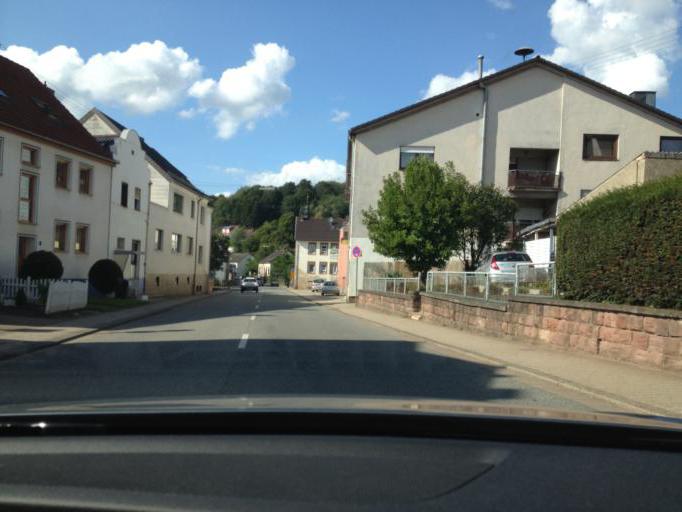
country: DE
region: Saarland
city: Eppelborn
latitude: 49.4159
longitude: 7.0156
